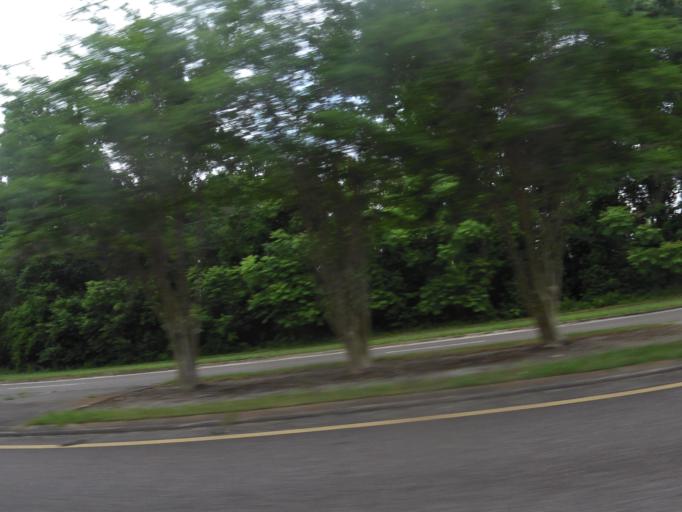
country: US
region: Florida
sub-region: Clay County
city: Bellair-Meadowbrook Terrace
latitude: 30.2906
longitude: -81.7657
